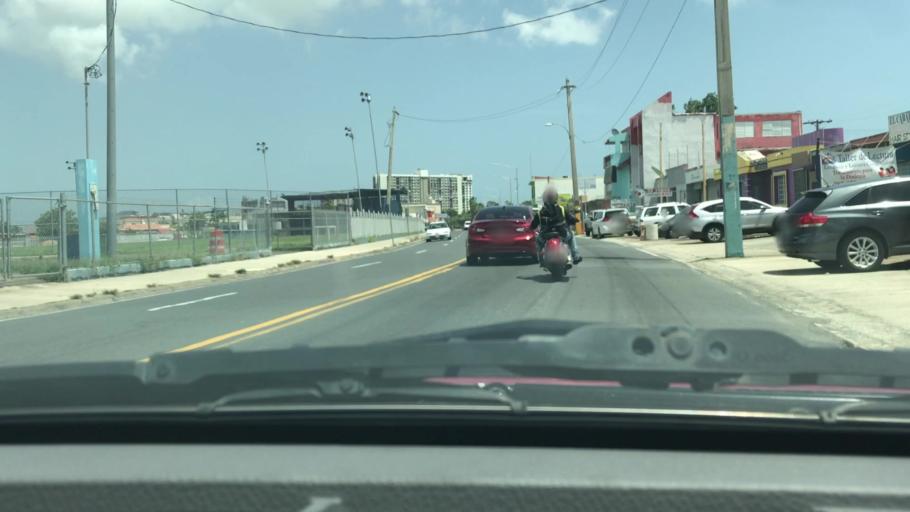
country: PR
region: Bayamon
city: Bayamon
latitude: 18.3908
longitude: -66.1413
